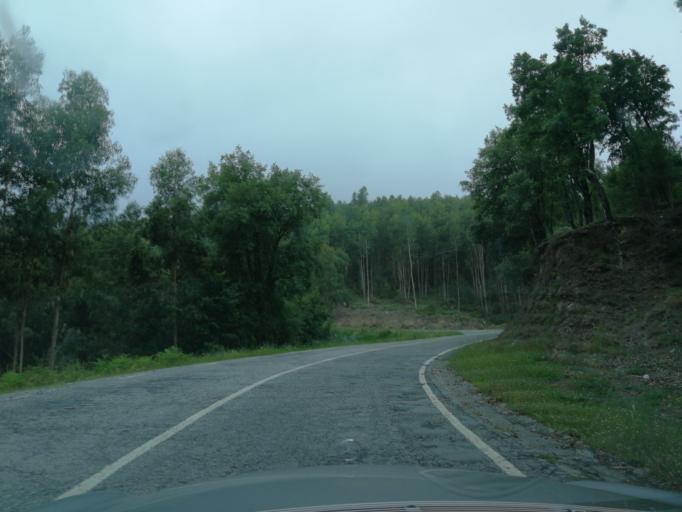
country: PT
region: Braga
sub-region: Braga
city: Braga
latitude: 41.5172
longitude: -8.3738
